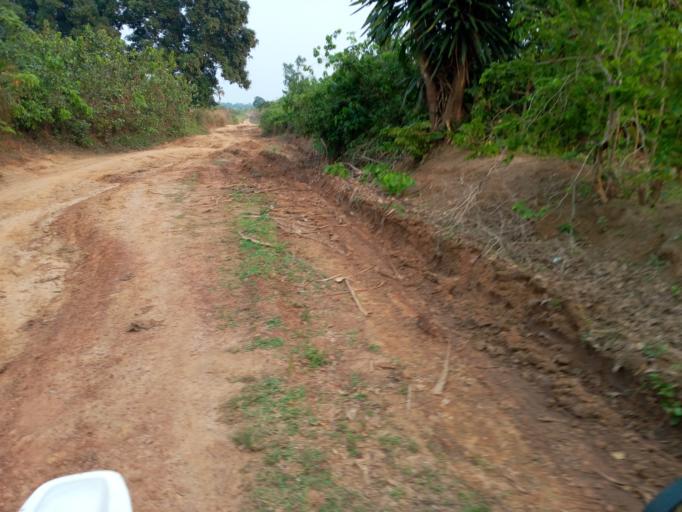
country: CD
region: Bandundu
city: Bandundu
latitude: -3.4416
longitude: 17.6050
